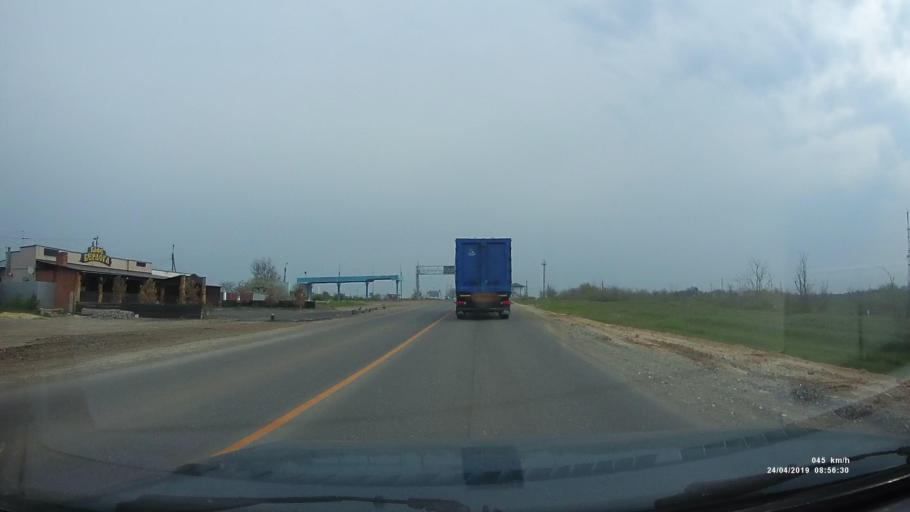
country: RU
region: Kalmykiya
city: Arshan'
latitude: 46.3016
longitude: 44.1856
